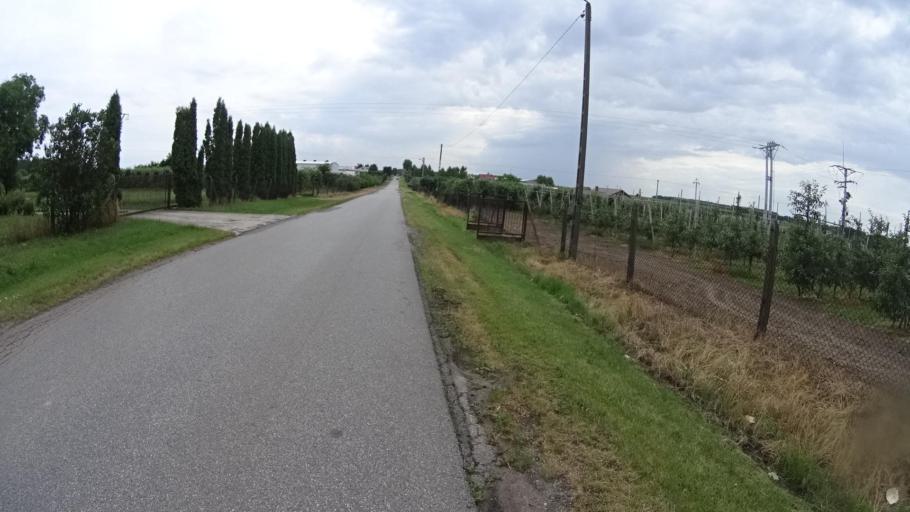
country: PL
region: Masovian Voivodeship
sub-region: Powiat grojecki
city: Belsk Duzy
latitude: 51.7971
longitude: 20.8586
